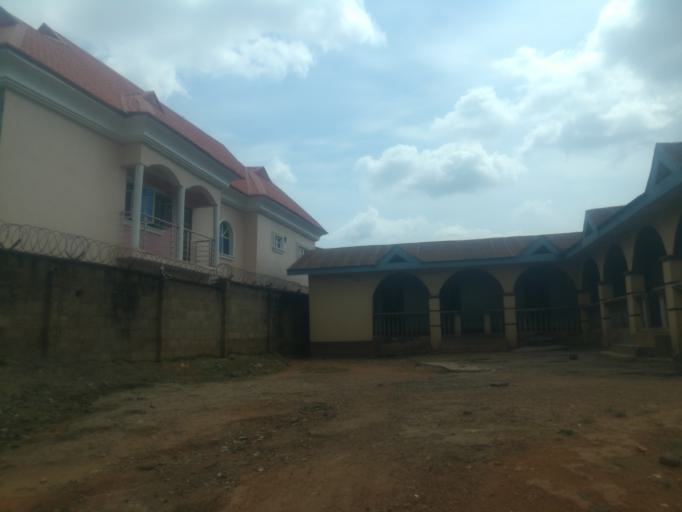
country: NG
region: Oyo
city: Ibadan
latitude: 7.4030
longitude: 3.9270
